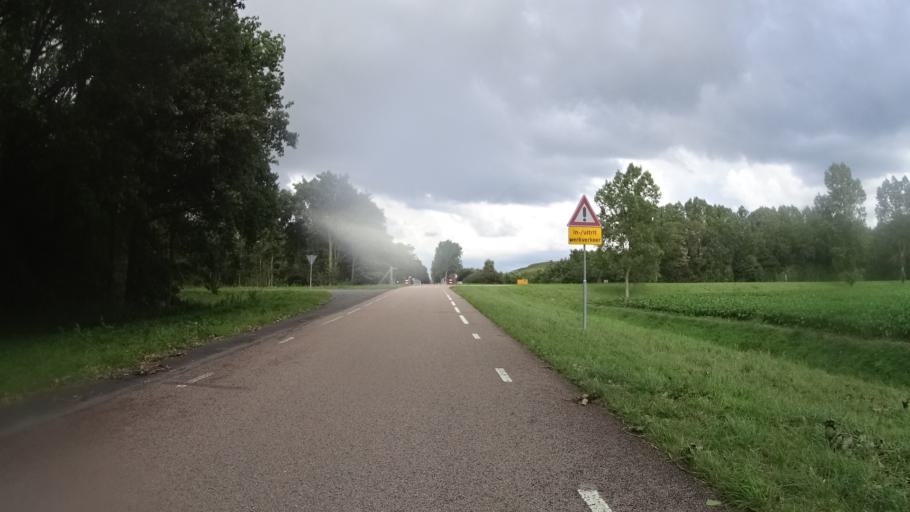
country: NL
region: North Holland
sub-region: Gemeente Hollands Kroon
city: Den Oever
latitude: 52.8995
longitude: 5.0354
